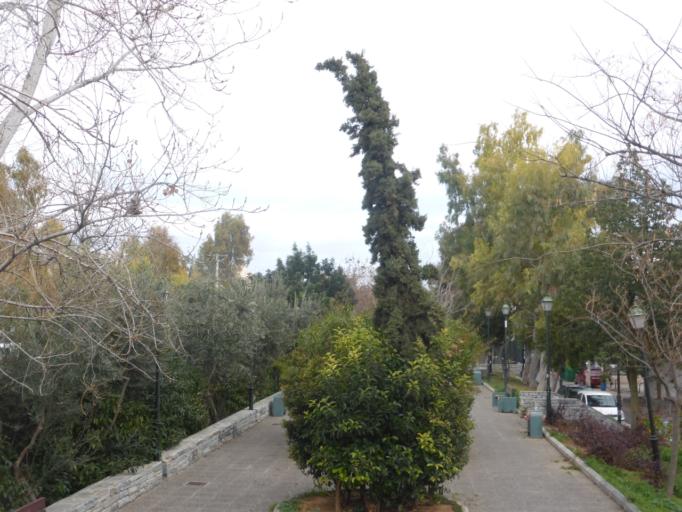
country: GR
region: Attica
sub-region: Nomarchia Athinas
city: Kallithea
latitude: 37.9562
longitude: 23.6929
